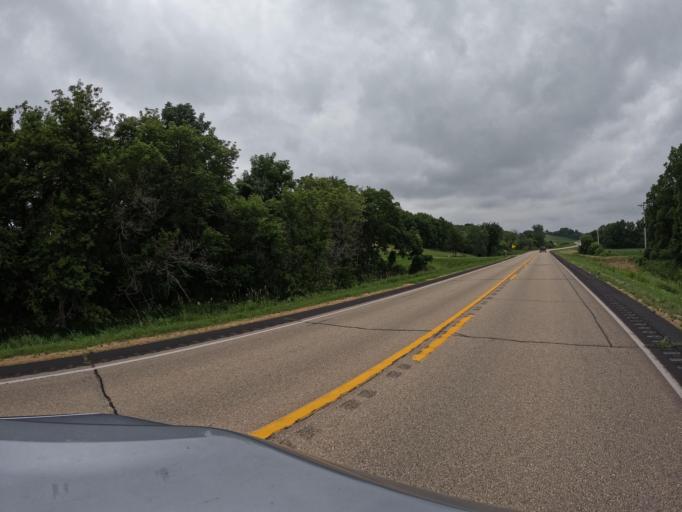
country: US
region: Illinois
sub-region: Carroll County
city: Savanna
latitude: 42.0218
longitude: -90.1839
